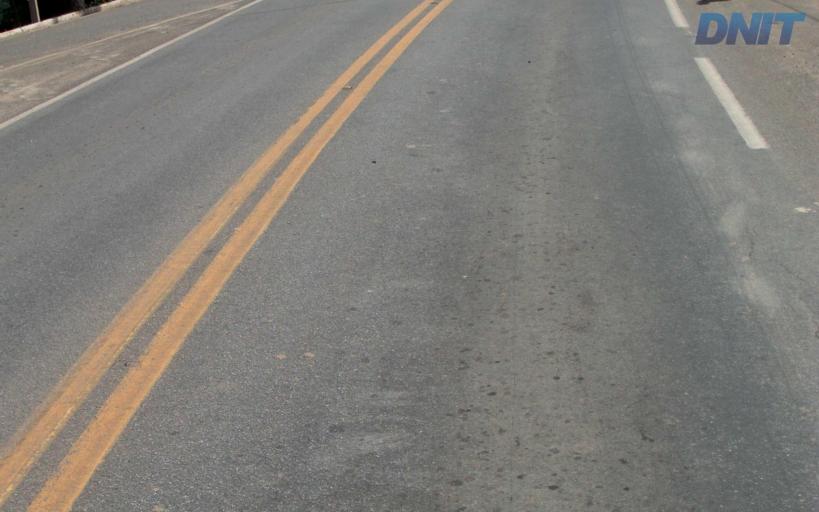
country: BR
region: Minas Gerais
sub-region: Belo Oriente
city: Belo Oriente
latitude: -19.1564
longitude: -42.2375
